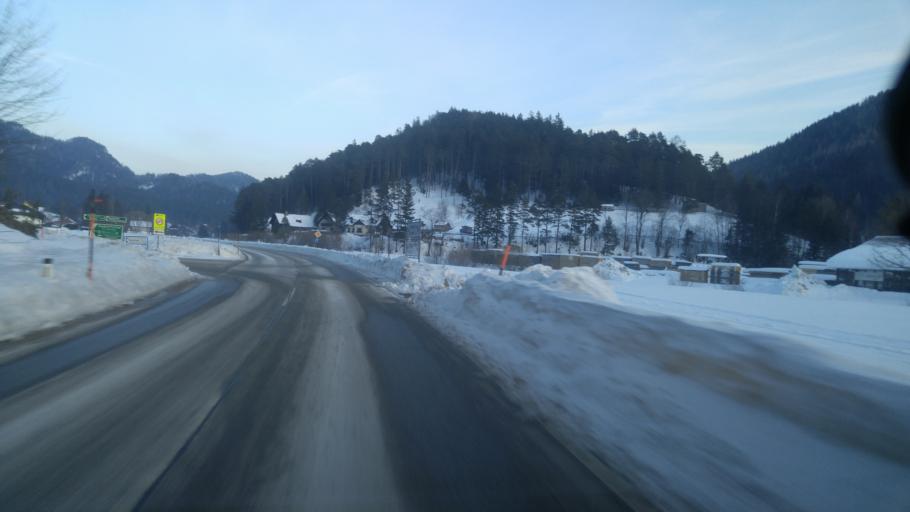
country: AT
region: Lower Austria
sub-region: Politischer Bezirk Wiener Neustadt
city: Rohr im Gebirge
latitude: 47.8943
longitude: 15.7299
